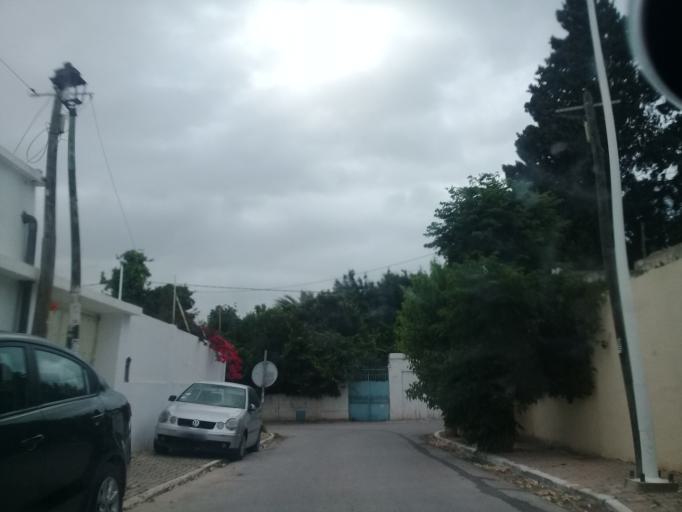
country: TN
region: Tunis
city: Sidi Bou Said
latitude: 36.8674
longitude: 10.3366
